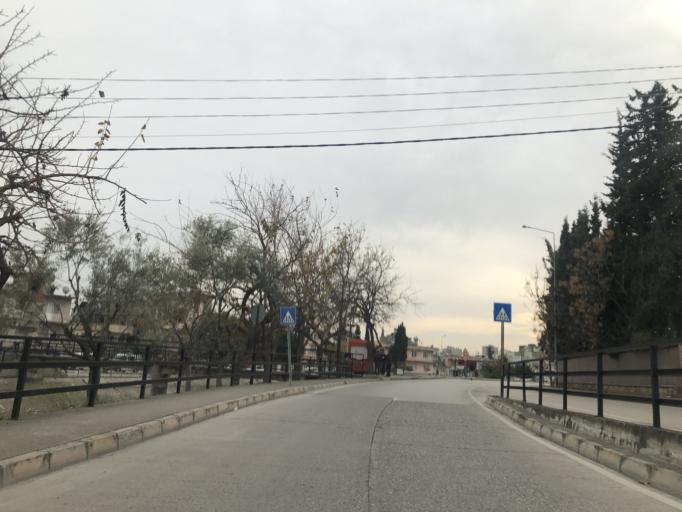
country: TR
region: Adana
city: Adana
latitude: 37.0106
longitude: 35.3277
